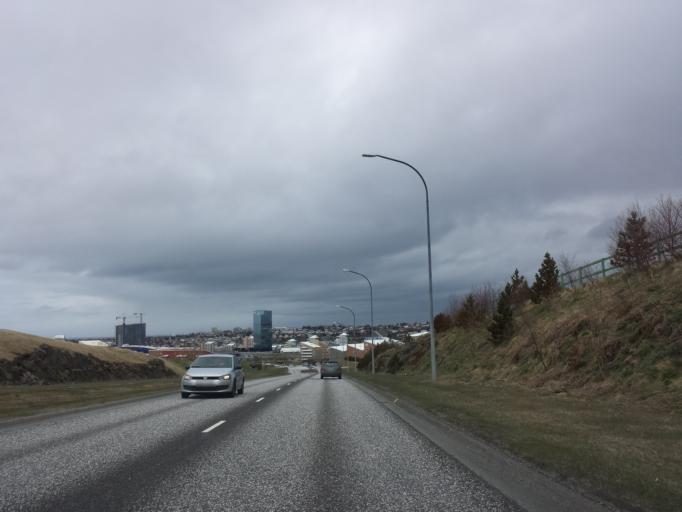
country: IS
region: Capital Region
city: Reykjavik
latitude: 64.0954
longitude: -21.8635
